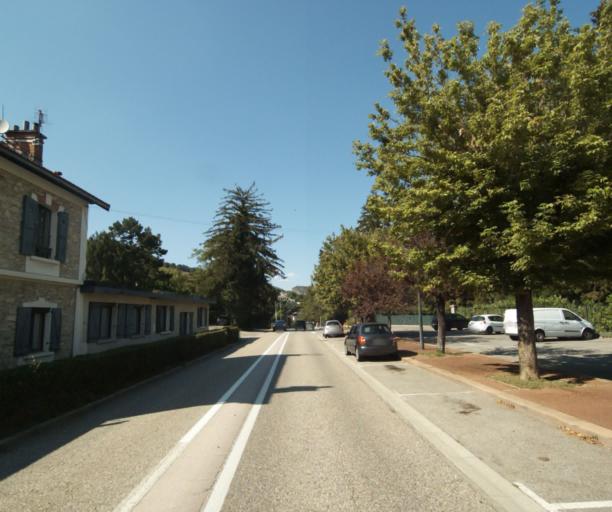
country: FR
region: Rhone-Alpes
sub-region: Departement de l'Isere
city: Seyssins
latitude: 45.1582
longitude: 5.6821
